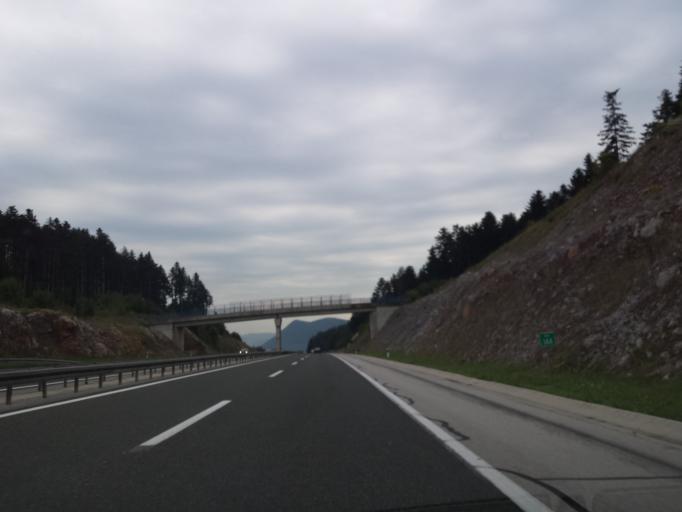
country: HR
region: Licko-Senjska
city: Otocac
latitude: 44.8501
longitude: 15.2306
